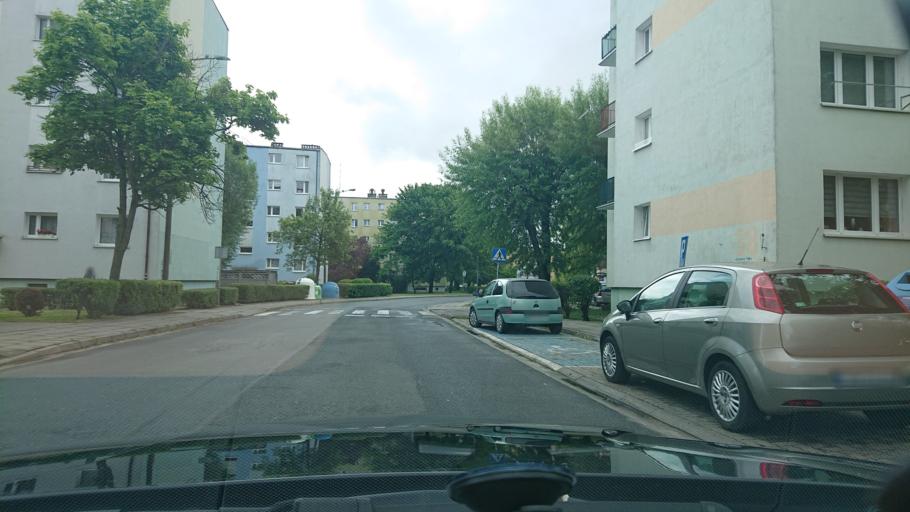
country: PL
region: Greater Poland Voivodeship
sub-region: Powiat gnieznienski
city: Gniezno
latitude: 52.5420
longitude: 17.6204
